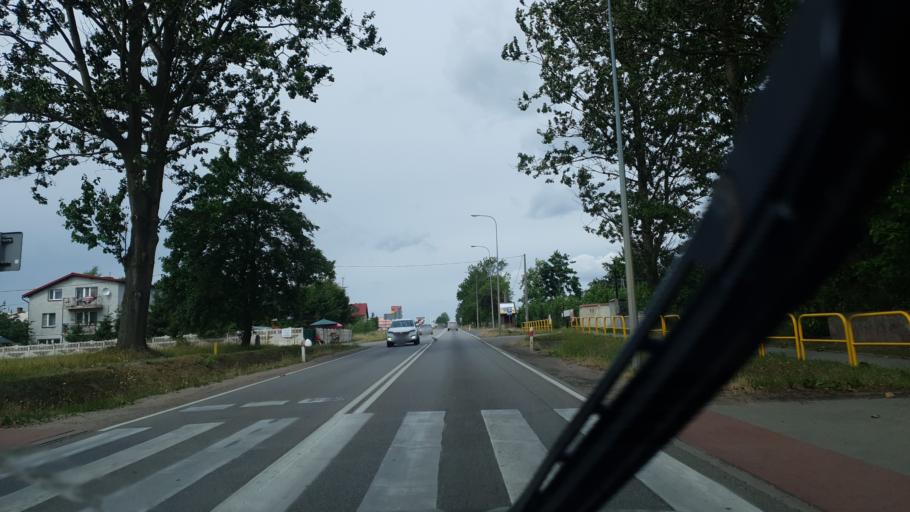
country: PL
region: Pomeranian Voivodeship
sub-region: Powiat kartuski
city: Banino
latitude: 54.4168
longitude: 18.3761
